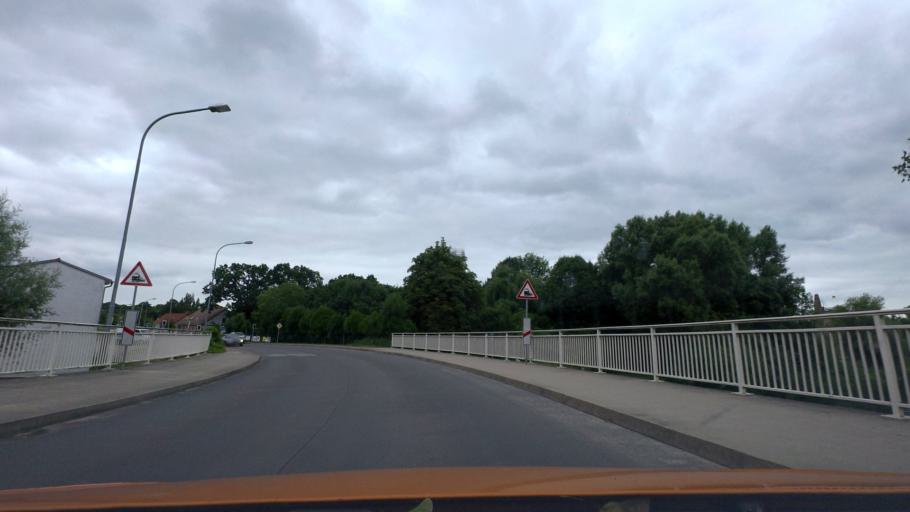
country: DE
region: Brandenburg
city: Wriezen
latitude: 52.7238
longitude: 14.1413
